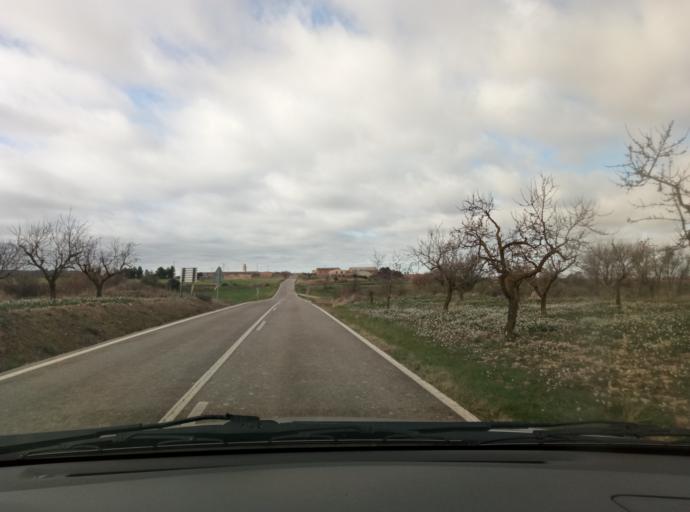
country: ES
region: Catalonia
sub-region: Provincia de Lleida
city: Vallbona de les Monges
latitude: 41.5624
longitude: 1.0698
